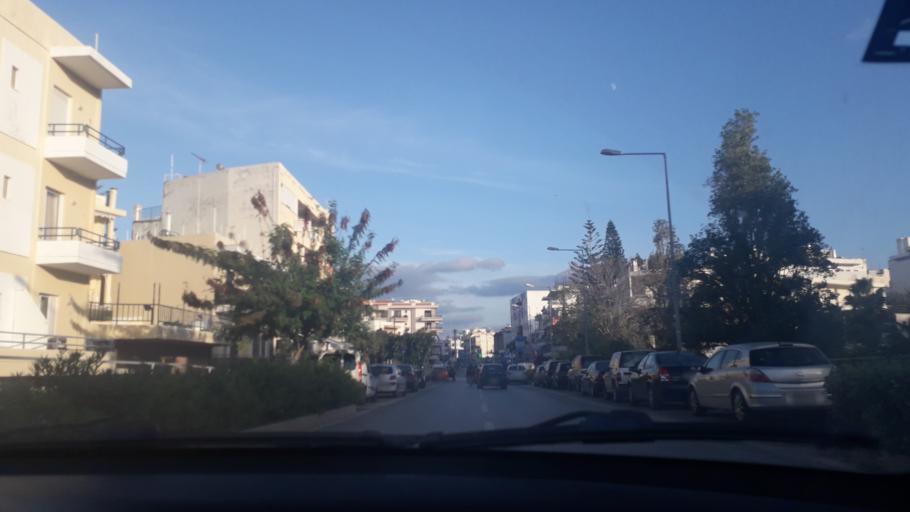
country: GR
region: Crete
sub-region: Nomos Rethymnis
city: Rethymno
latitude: 35.3646
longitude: 24.4833
